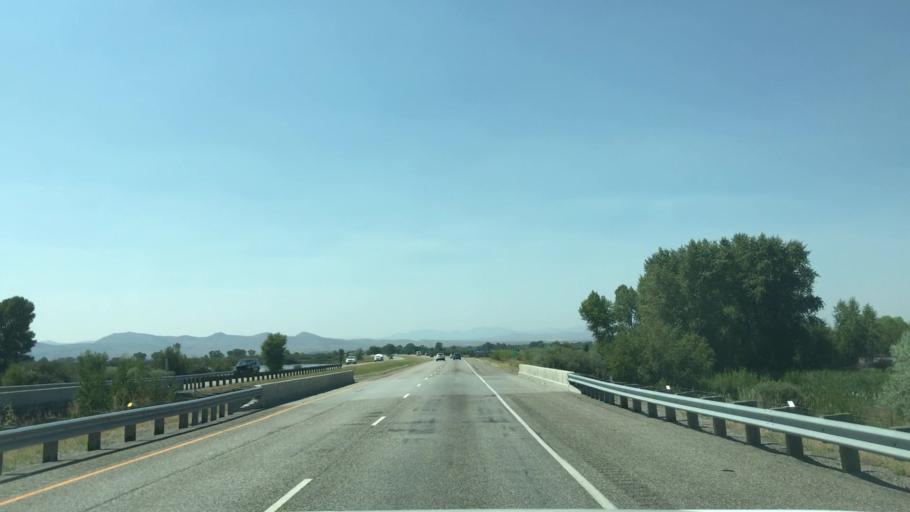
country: US
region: Montana
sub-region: Gallatin County
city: Three Forks
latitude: 45.8964
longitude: -111.4988
